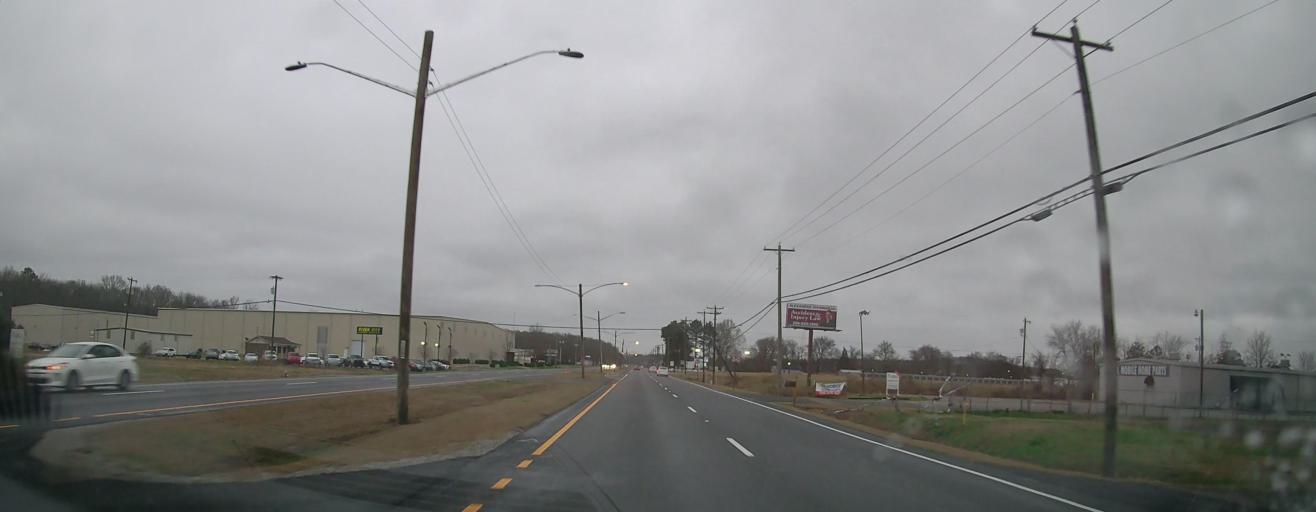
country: US
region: Alabama
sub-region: Morgan County
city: Flint City
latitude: 34.5446
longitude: -86.9739
